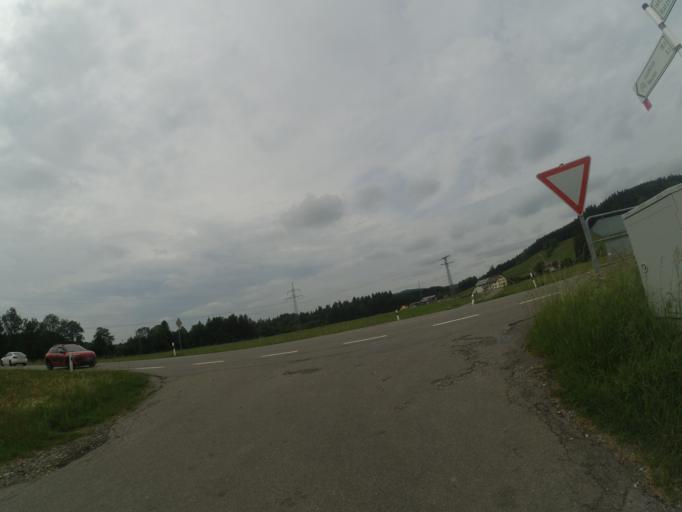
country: DE
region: Baden-Wuerttemberg
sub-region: Tuebingen Region
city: Isny im Allgau
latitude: 47.7161
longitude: 10.0539
